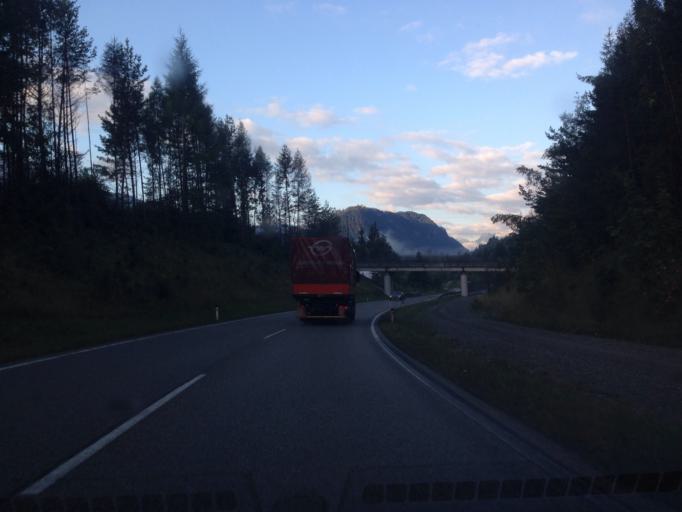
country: AT
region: Tyrol
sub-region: Politischer Bezirk Reutte
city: Breitenwang
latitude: 47.4864
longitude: 10.7426
